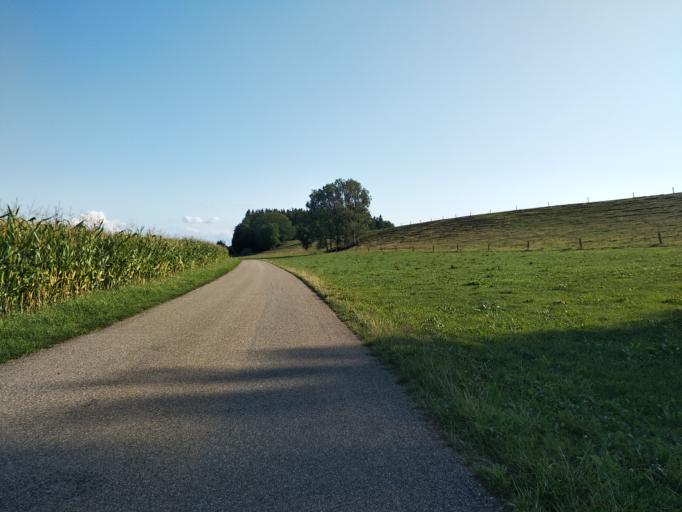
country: DE
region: Bavaria
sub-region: Swabia
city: Lautrach
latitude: 47.8829
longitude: 10.1158
